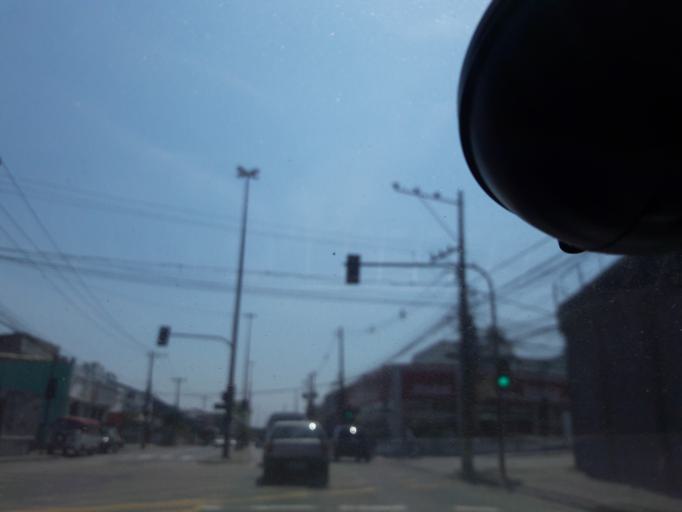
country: BR
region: Rio de Janeiro
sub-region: Sao Joao De Meriti
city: Sao Joao de Meriti
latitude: -22.8776
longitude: -43.3635
